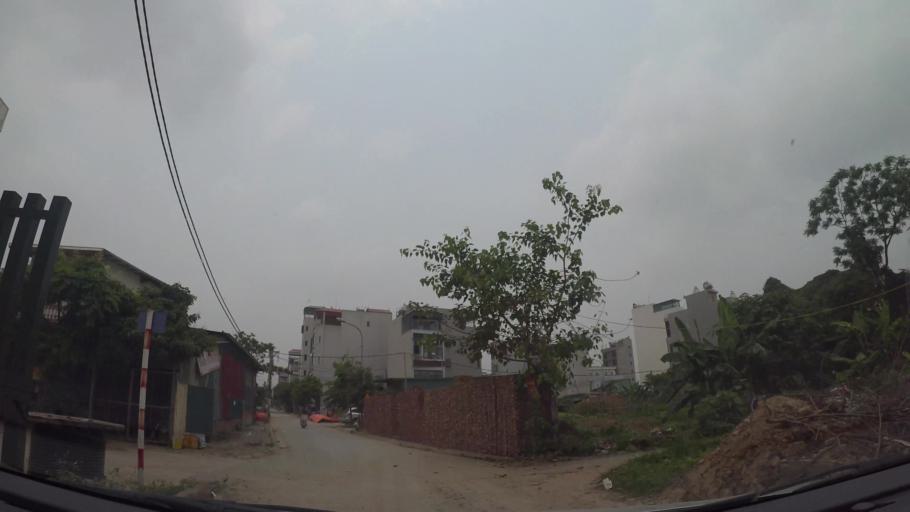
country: VN
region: Ha Noi
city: Ha Dong
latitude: 20.9884
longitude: 105.7434
